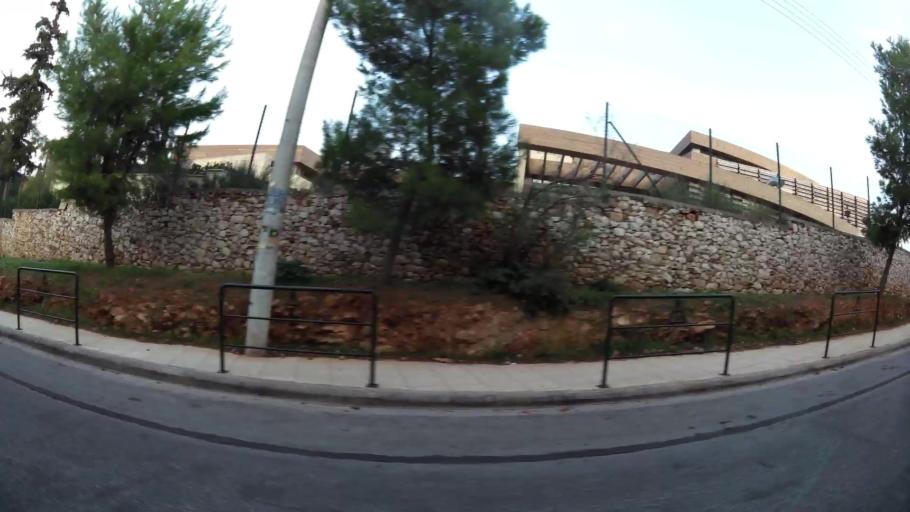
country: GR
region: Attica
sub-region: Nomarchia Athinas
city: Psychiko
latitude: 38.0178
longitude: 23.7774
